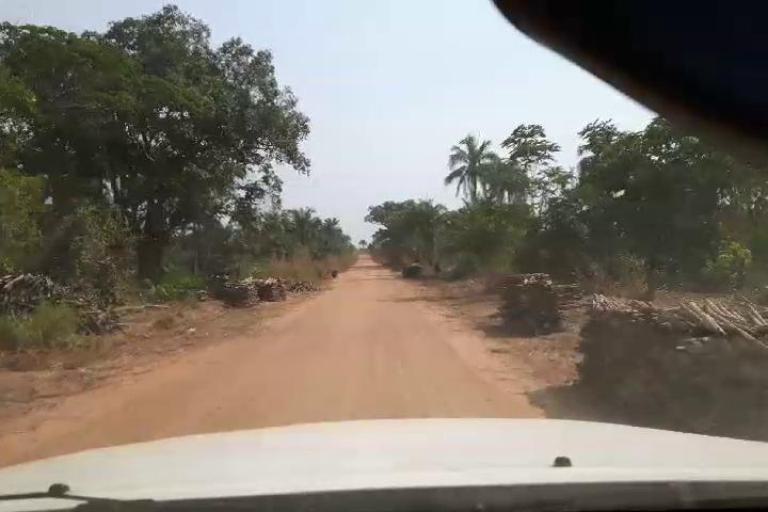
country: SL
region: Northern Province
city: Masingbi
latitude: 8.7970
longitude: -11.8675
